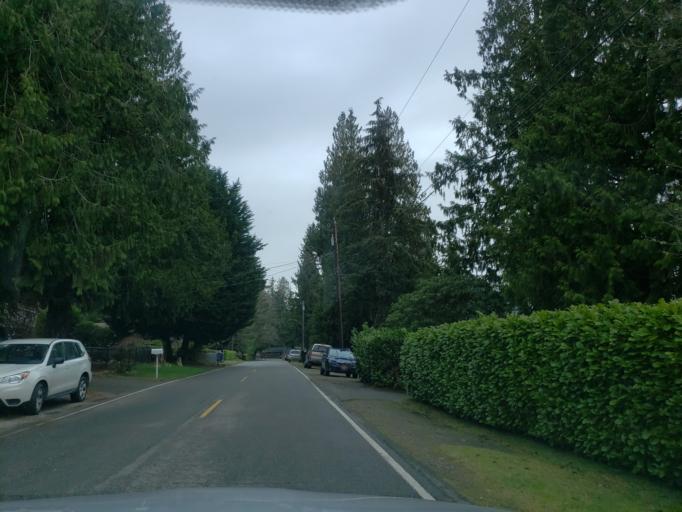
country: US
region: Washington
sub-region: Snohomish County
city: Meadowdale
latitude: 47.8270
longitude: -122.3450
